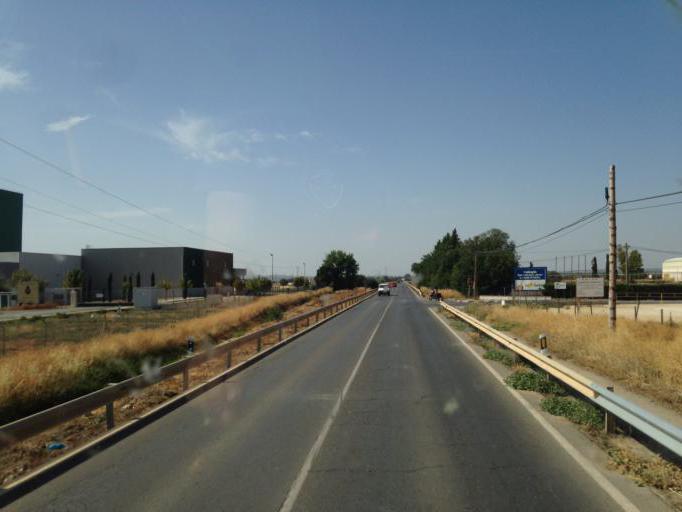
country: ES
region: Andalusia
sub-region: Provincia de Malaga
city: Antequera
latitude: 37.0361
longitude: -4.5613
